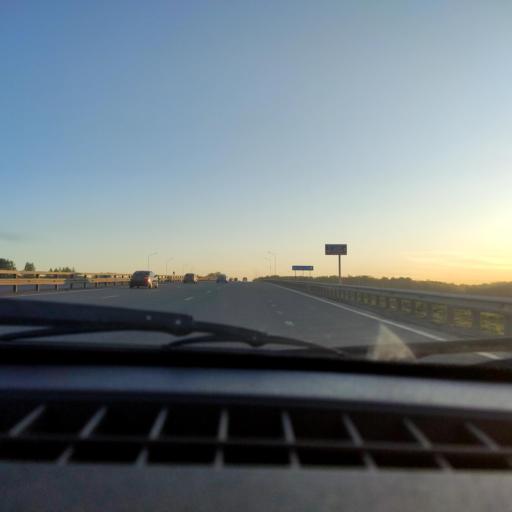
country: RU
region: Bashkortostan
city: Avdon
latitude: 54.6672
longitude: 55.7431
